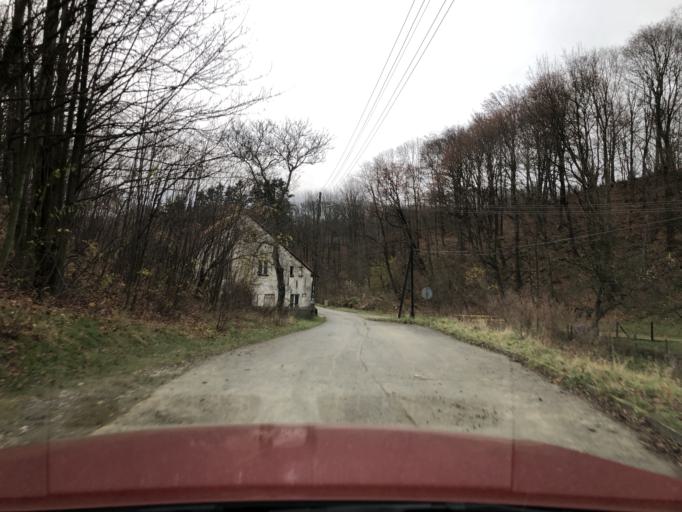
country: PL
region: Lower Silesian Voivodeship
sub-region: Powiat walbrzyski
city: Stare Bogaczowice
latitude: 50.8029
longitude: 16.1907
